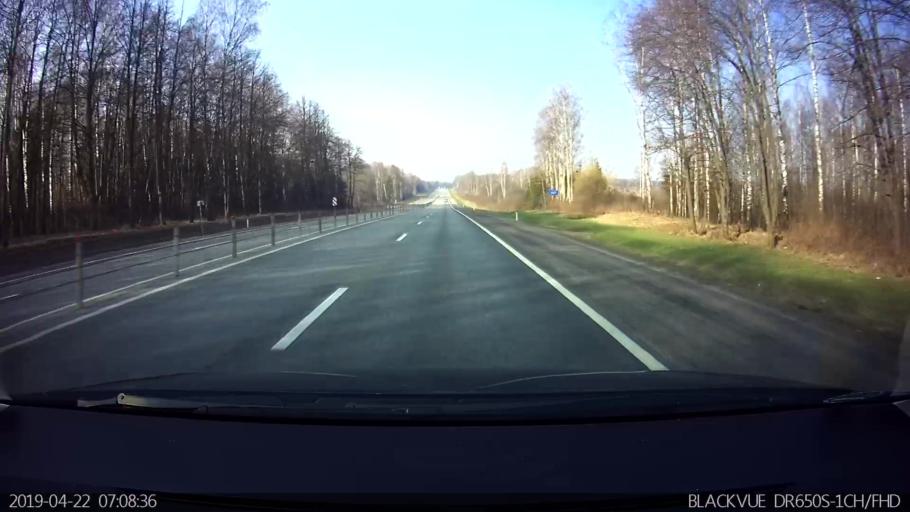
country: RU
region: Smolensk
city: Vyaz'ma
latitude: 55.3310
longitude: 34.5787
